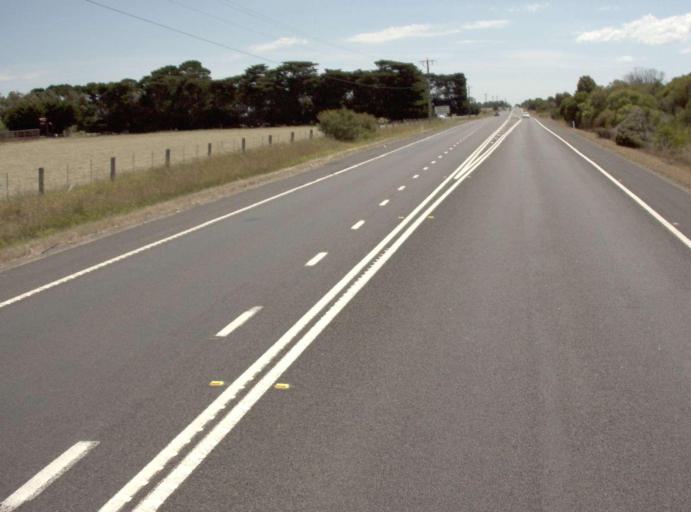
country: AU
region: Victoria
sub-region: Wellington
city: Sale
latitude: -38.1012
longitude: 146.9530
